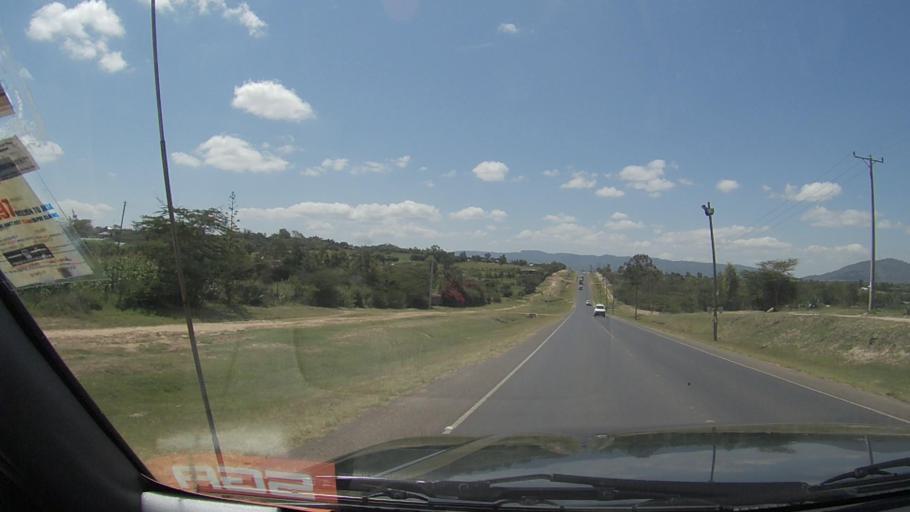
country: KE
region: Machakos
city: Machakos
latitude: -1.5307
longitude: 37.2028
